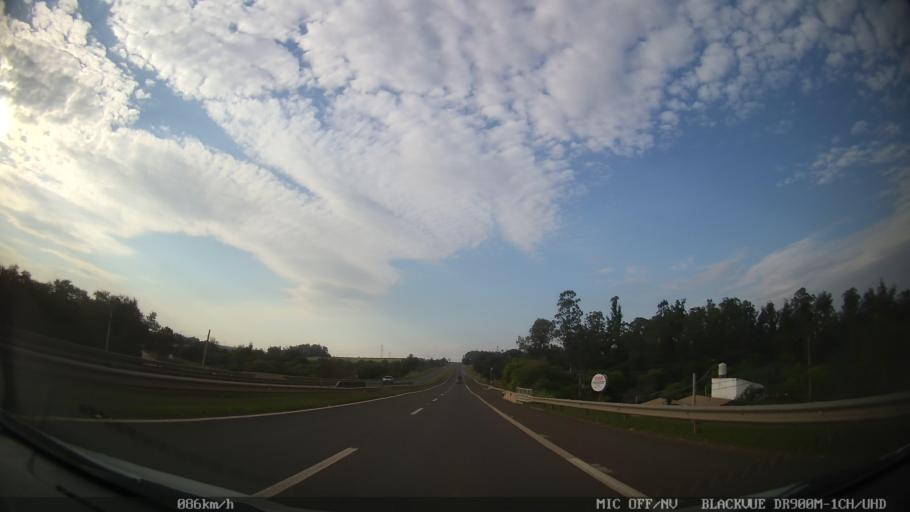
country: BR
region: Sao Paulo
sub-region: Cosmopolis
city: Cosmopolis
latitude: -22.6163
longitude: -47.1972
